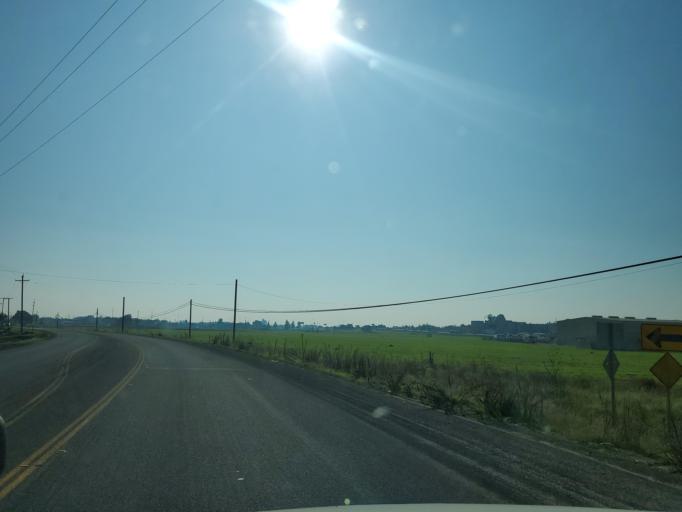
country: US
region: California
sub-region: San Joaquin County
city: French Camp
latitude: 37.8938
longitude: -121.2799
